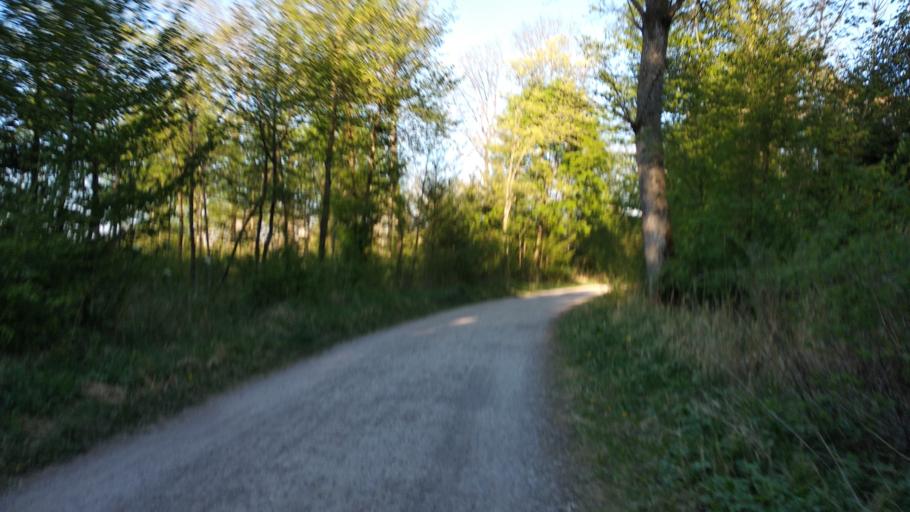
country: DE
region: Bavaria
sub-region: Upper Bavaria
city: Haar
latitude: 48.0945
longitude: 11.7204
